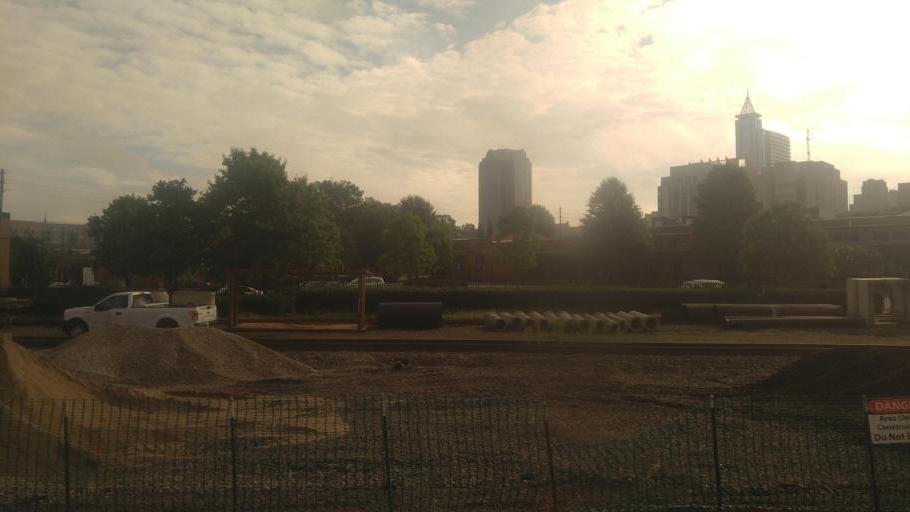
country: US
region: North Carolina
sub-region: Wake County
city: Raleigh
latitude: 35.7751
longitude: -78.6458
